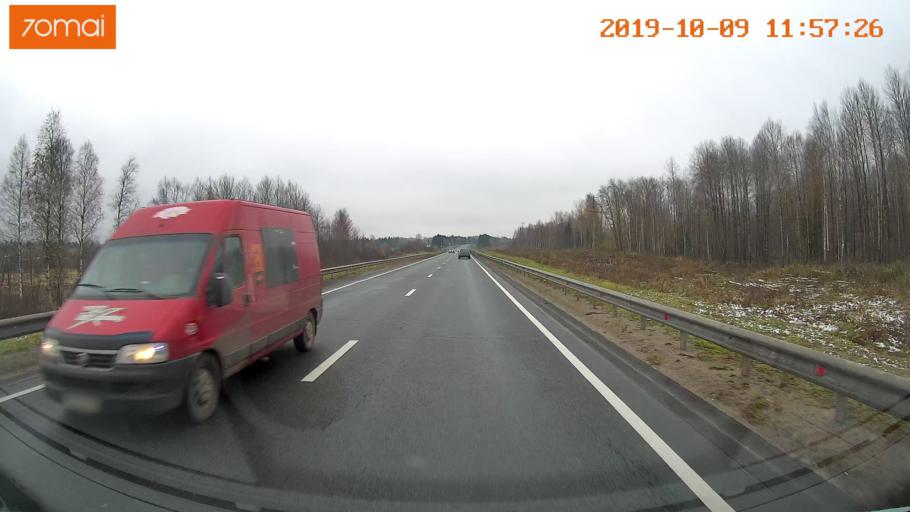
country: RU
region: Vologda
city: Gryazovets
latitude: 58.7323
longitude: 40.2926
